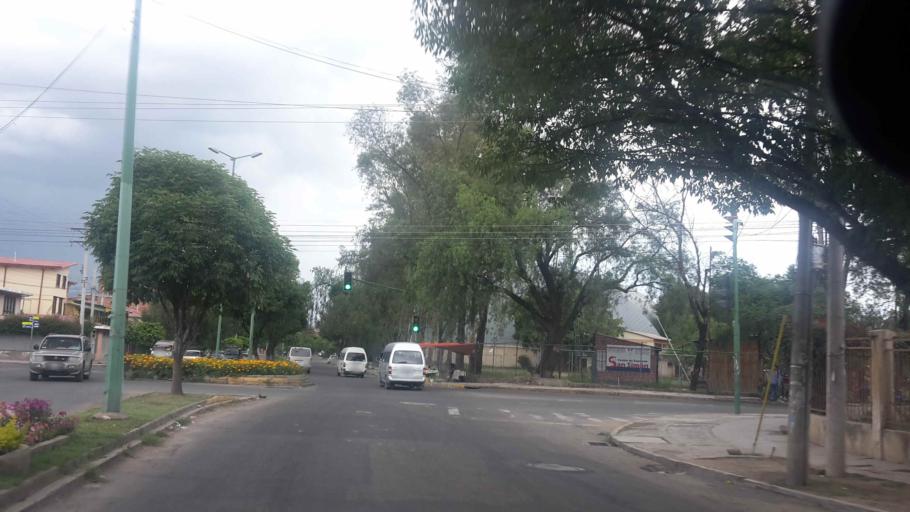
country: BO
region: Cochabamba
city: Cochabamba
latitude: -17.3933
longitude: -66.1416
